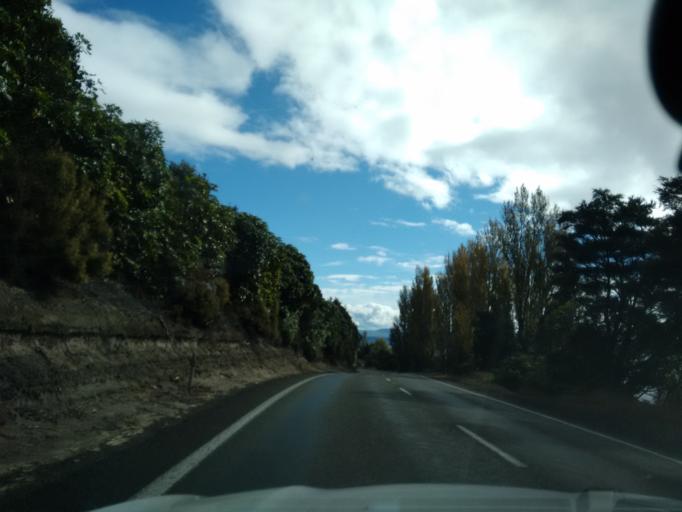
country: NZ
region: Waikato
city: Turangi
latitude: -38.8801
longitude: 175.9765
